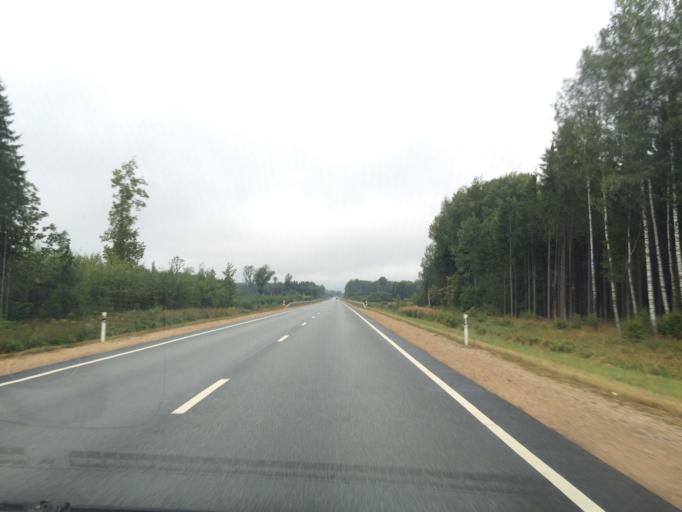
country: LV
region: Lielvarde
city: Lielvarde
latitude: 56.8190
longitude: 24.8159
